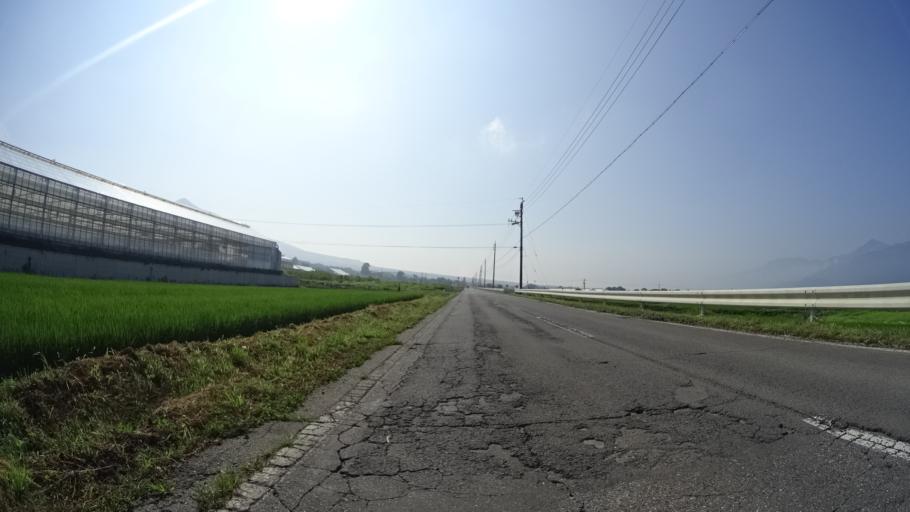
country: JP
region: Nagano
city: Chino
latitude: 35.9409
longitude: 138.2525
